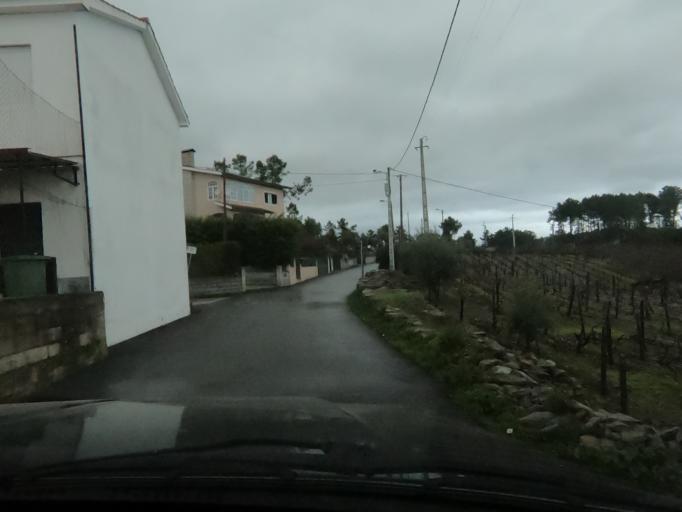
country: PT
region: Vila Real
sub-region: Vila Real
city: Vila Real
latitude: 41.2627
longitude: -7.7346
